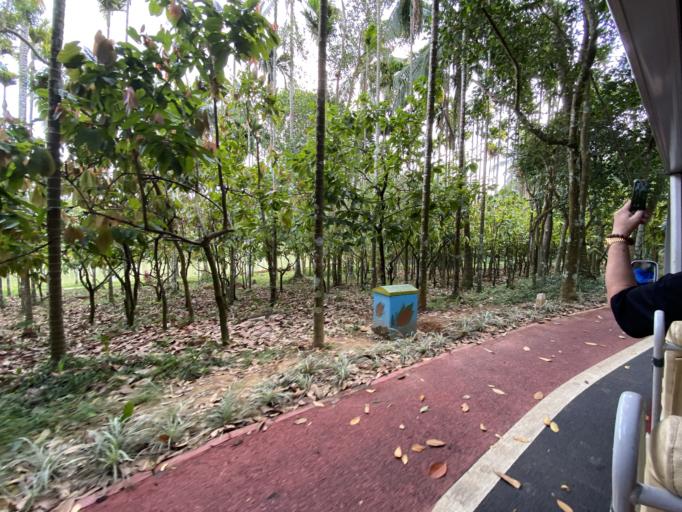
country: CN
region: Hainan
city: Nanqiao
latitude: 18.7334
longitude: 110.1909
